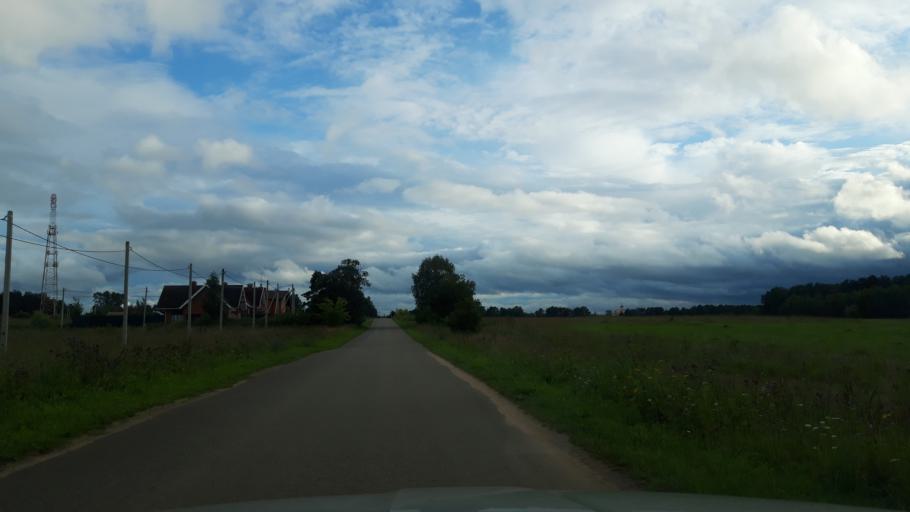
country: RU
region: Moskovskaya
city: Istra
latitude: 56.0985
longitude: 36.7996
